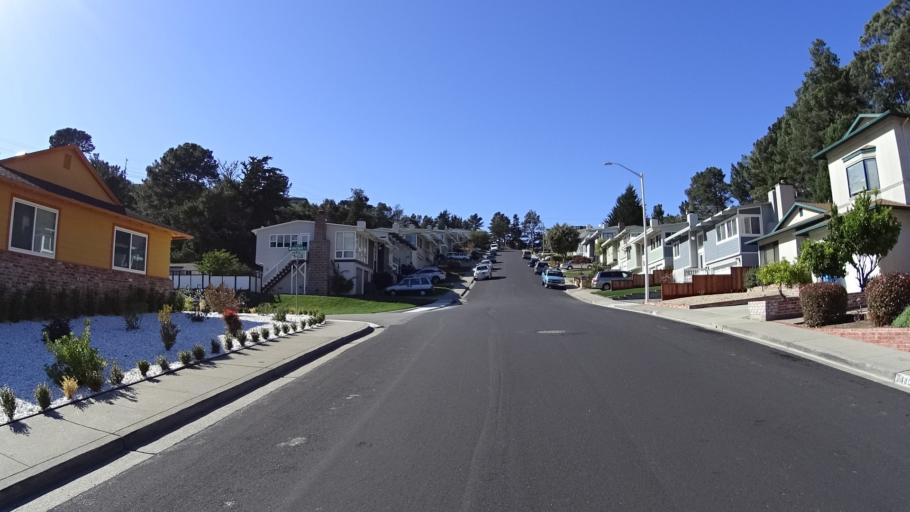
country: US
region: California
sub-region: San Mateo County
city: San Bruno
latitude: 37.6186
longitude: -122.4351
